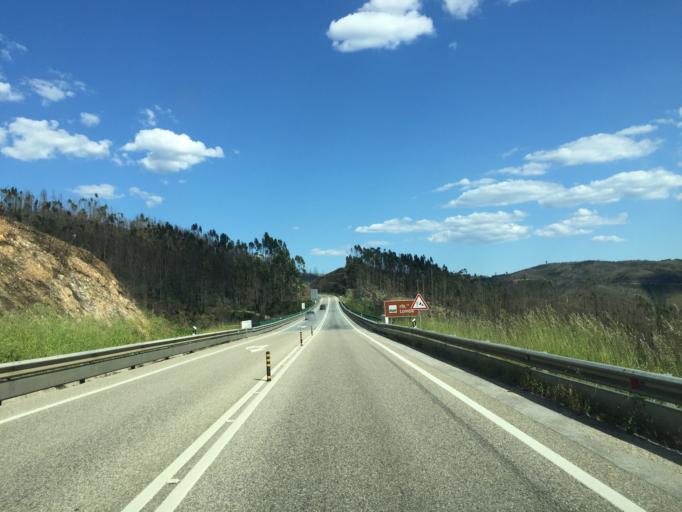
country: PT
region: Leiria
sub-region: Figueiro Dos Vinhos
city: Figueiro dos Vinhos
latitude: 39.9271
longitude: -8.3251
